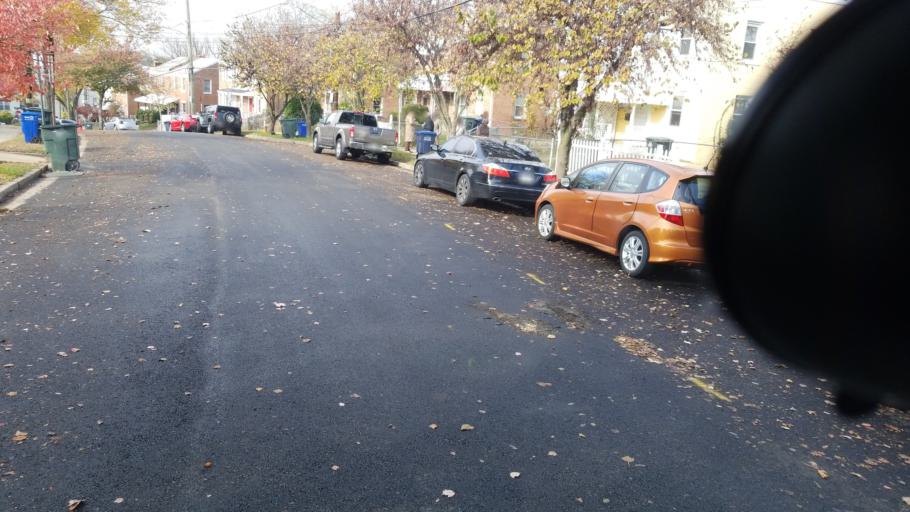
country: US
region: Maryland
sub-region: Prince George's County
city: Capitol Heights
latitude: 38.8887
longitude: -76.9348
